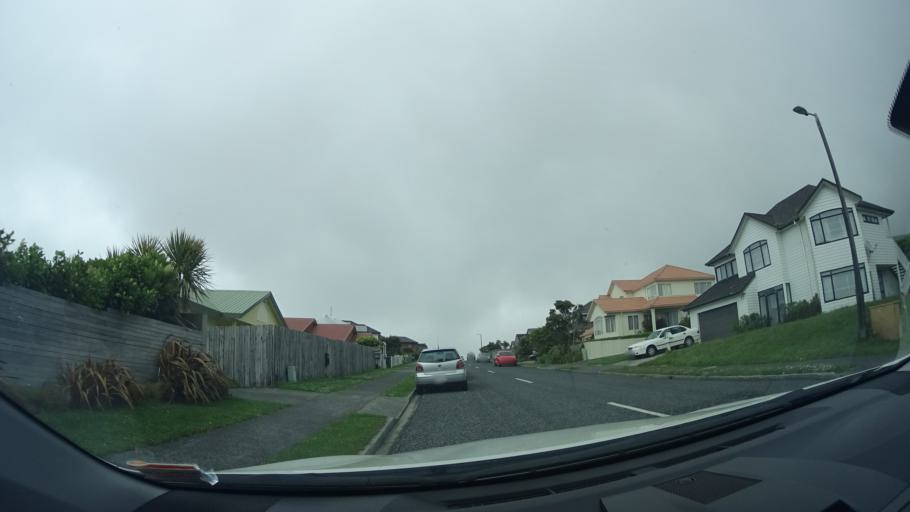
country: NZ
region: Wellington
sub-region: Wellington City
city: Brooklyn
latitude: -41.3062
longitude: 174.7534
